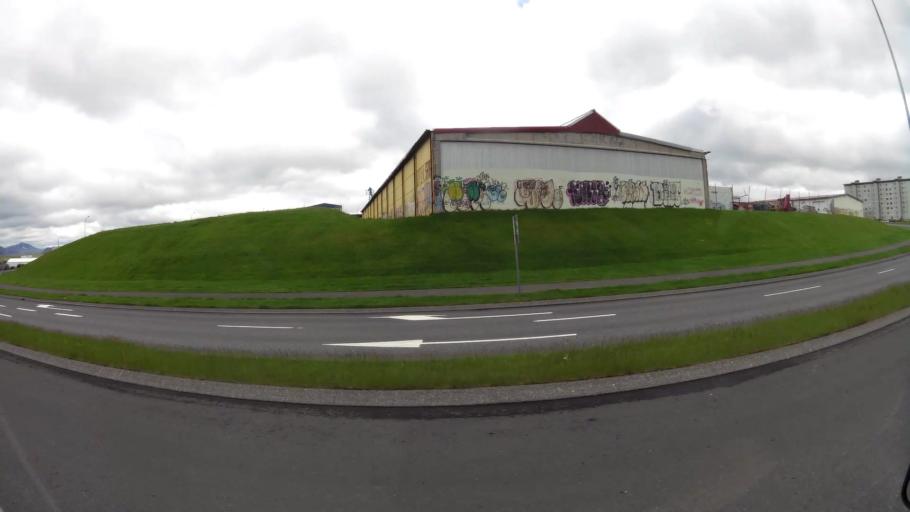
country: IS
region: Capital Region
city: Reykjavik
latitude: 64.1540
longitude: -21.8814
